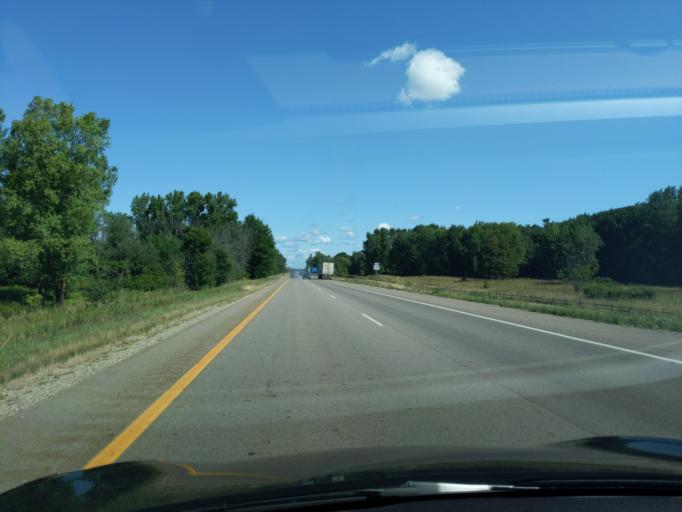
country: US
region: Michigan
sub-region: Gratiot County
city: Ithaca
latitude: 43.3270
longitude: -84.6010
